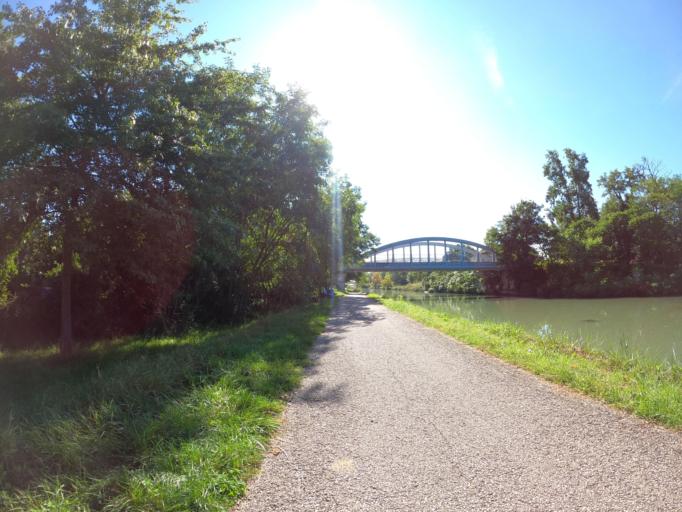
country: FR
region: Aquitaine
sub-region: Departement du Lot-et-Garonne
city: Bon-Encontre
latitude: 44.1791
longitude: 0.6622
